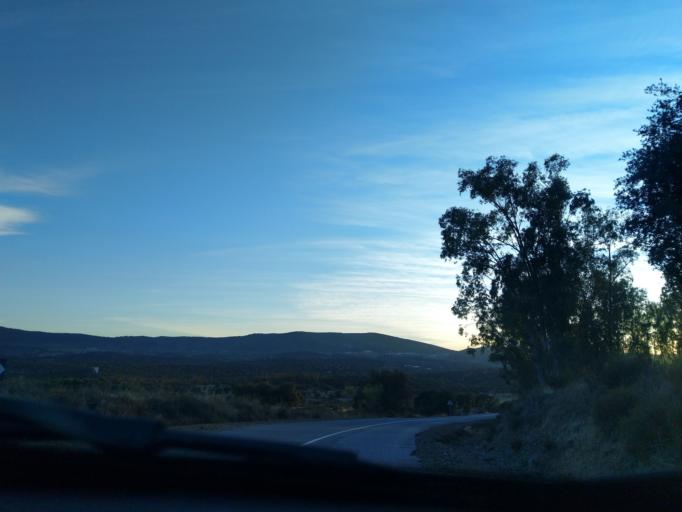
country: ES
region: Extremadura
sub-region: Provincia de Badajoz
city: Valverde de Llerena
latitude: 38.1833
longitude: -5.8616
